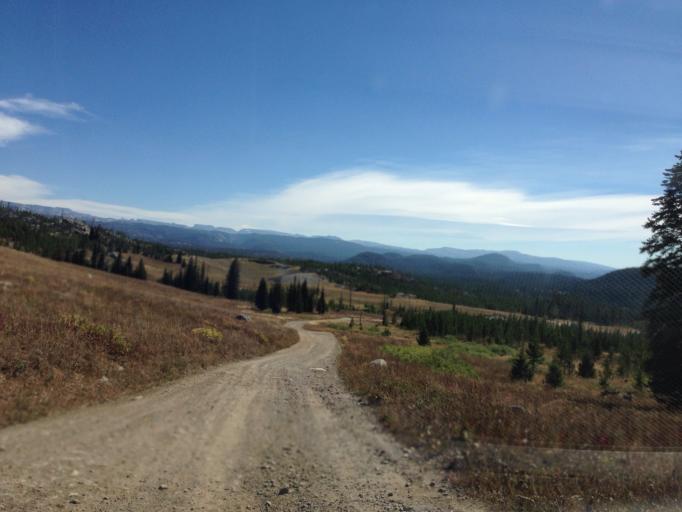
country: US
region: Montana
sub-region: Stillwater County
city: Absarokee
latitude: 45.0324
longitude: -109.9086
